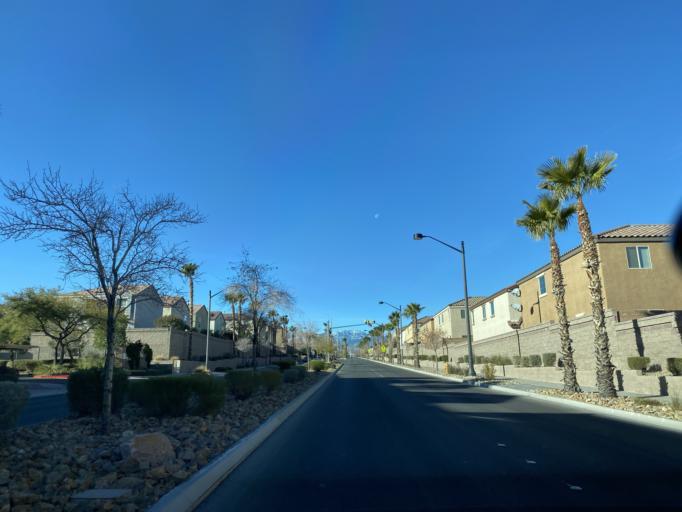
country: US
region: Nevada
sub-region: Clark County
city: Summerlin South
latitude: 36.2992
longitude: -115.2917
